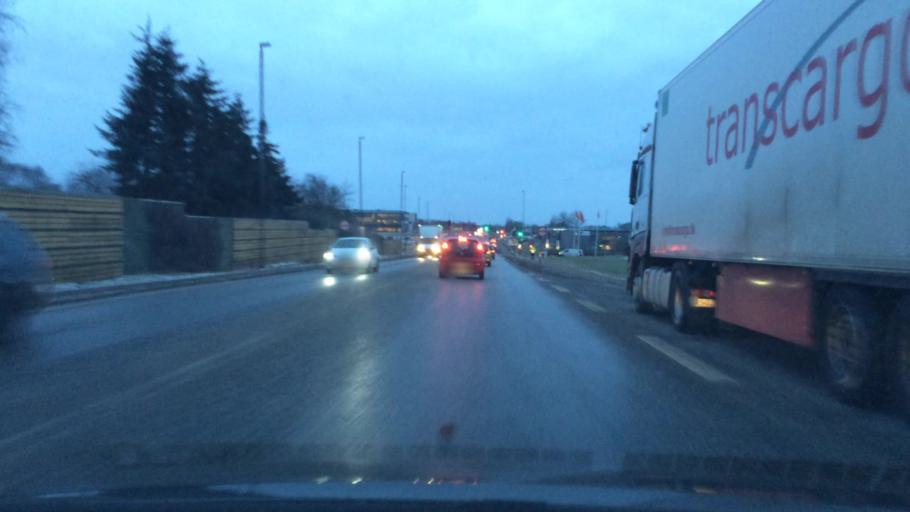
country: DK
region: Central Jutland
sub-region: Horsens Kommune
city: Horsens
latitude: 55.8348
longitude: 9.8091
